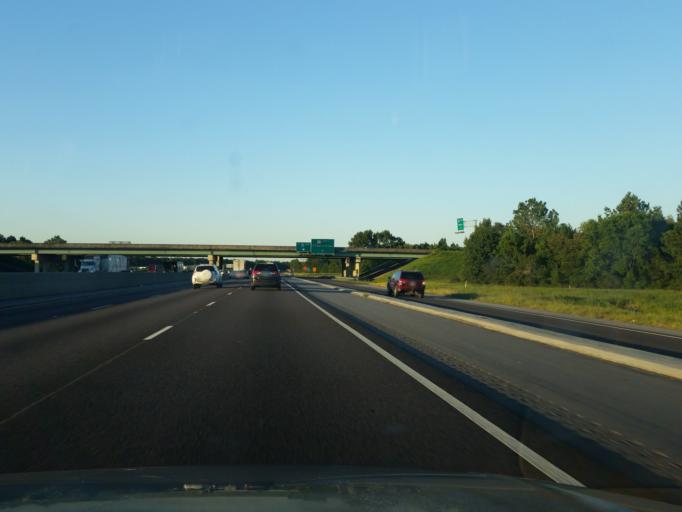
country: US
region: Alabama
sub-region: Mobile County
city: Tillmans Corner
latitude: 30.5940
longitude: -88.1552
